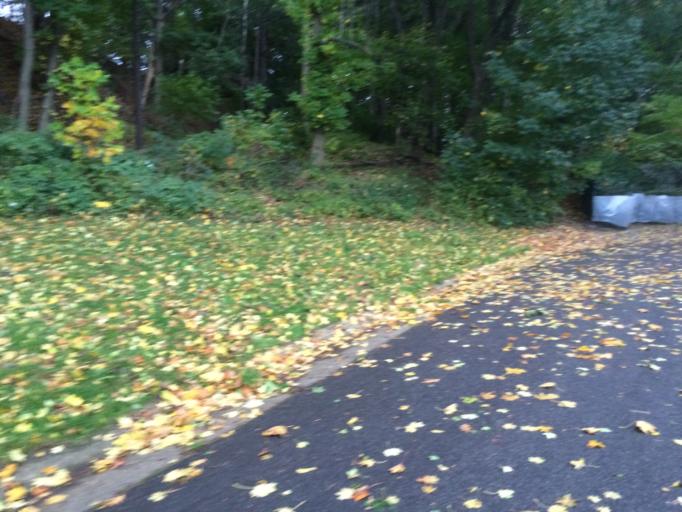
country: US
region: New York
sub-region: Monroe County
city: Rochester
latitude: 43.1336
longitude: -77.6034
